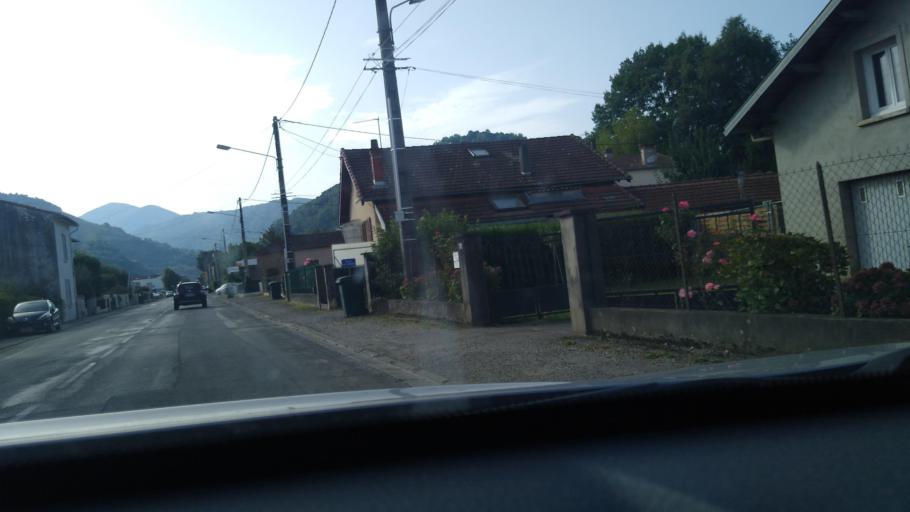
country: FR
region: Midi-Pyrenees
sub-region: Departement de l'Ariege
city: Saint-Girons
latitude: 42.9718
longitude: 1.1568
